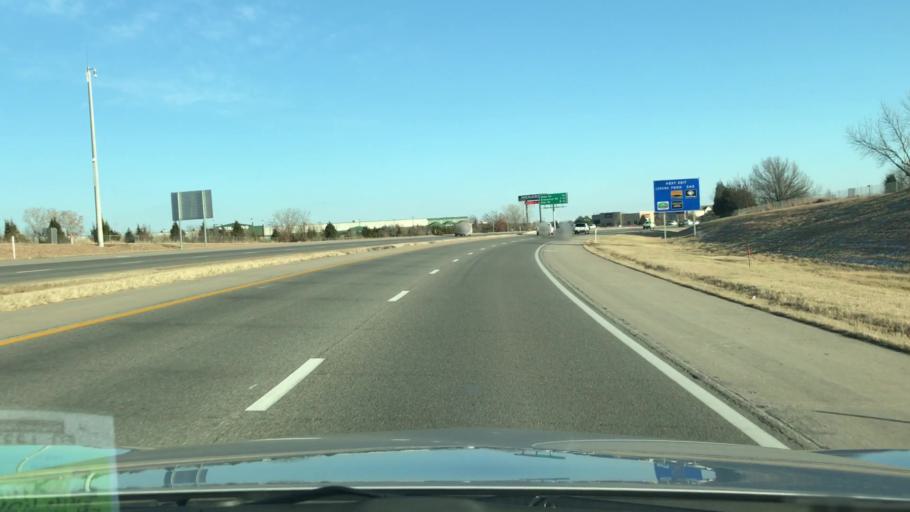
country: US
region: Kansas
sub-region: Sedgwick County
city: Bellaire
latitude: 37.7441
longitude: -97.2358
